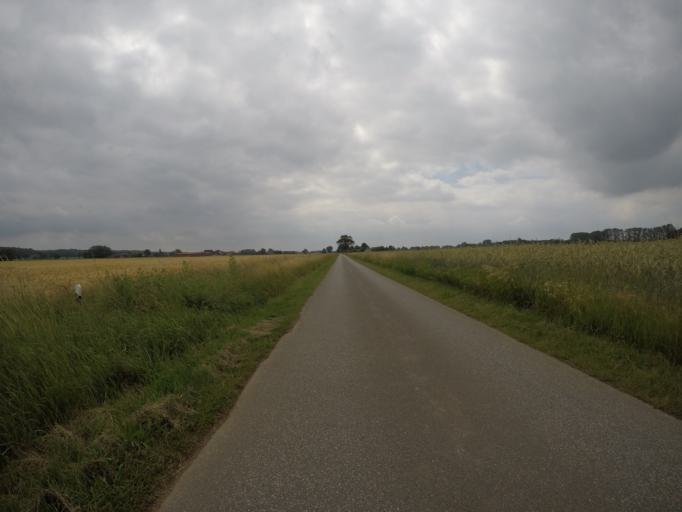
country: DE
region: North Rhine-Westphalia
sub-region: Regierungsbezirk Dusseldorf
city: Hamminkeln
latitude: 51.7432
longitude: 6.6363
